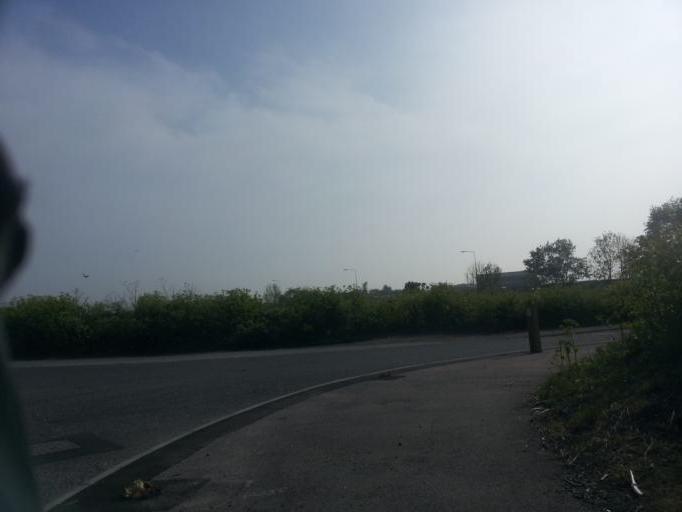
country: GB
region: England
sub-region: Kent
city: Queenborough
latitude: 51.4272
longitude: 0.7448
